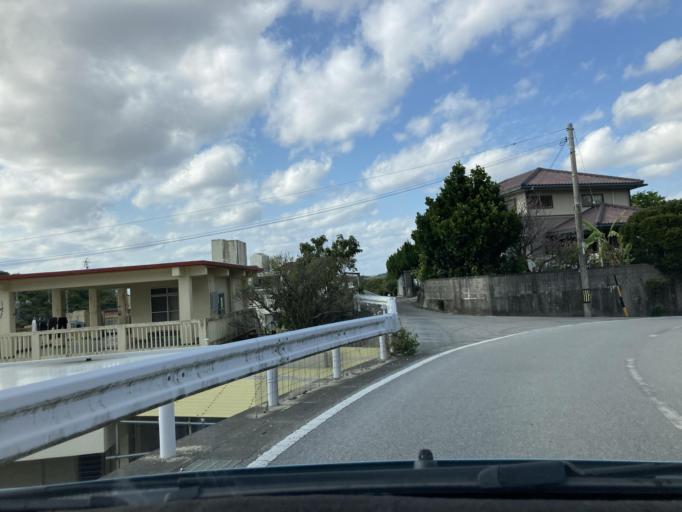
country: JP
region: Okinawa
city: Tomigusuku
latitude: 26.1868
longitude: 127.7570
